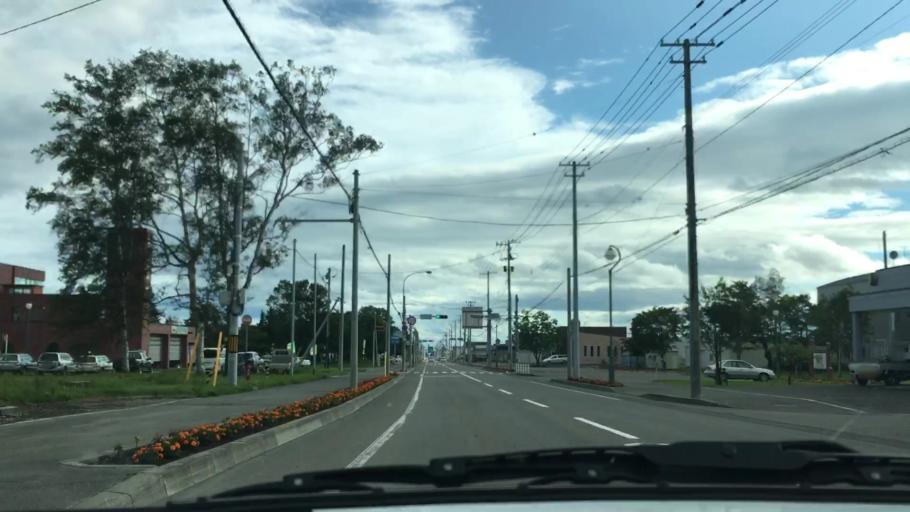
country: JP
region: Hokkaido
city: Otofuke
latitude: 43.2337
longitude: 143.2953
